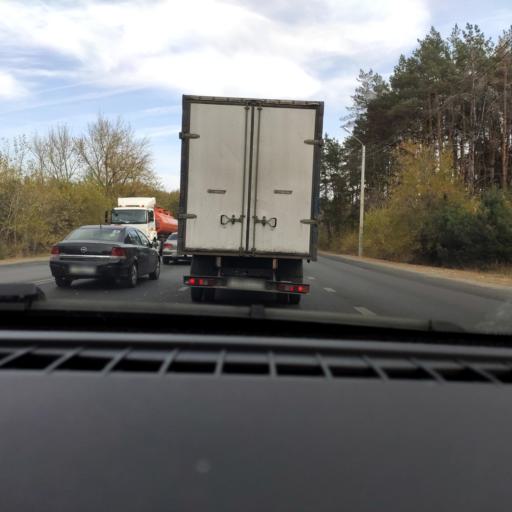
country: RU
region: Voronezj
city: Voronezh
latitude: 51.6814
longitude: 39.2765
